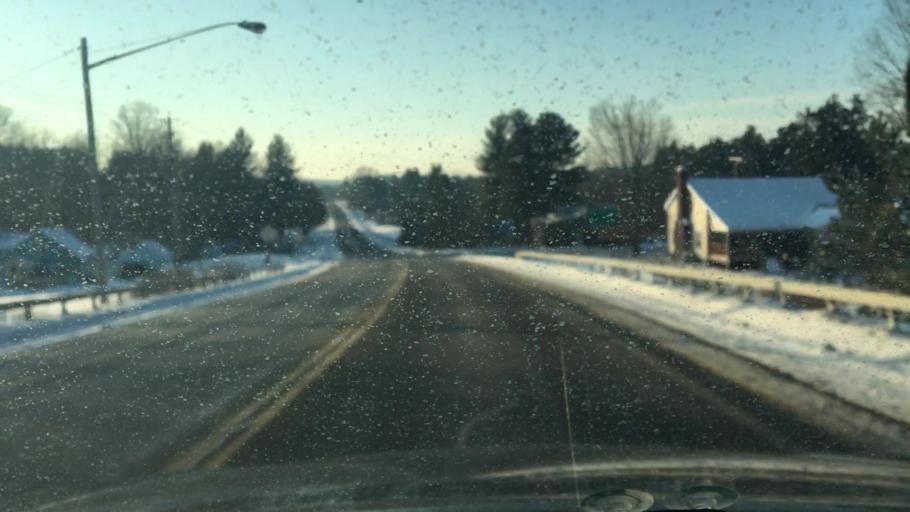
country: US
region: New York
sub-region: Chautauqua County
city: Lakewood
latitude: 42.0798
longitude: -79.3687
